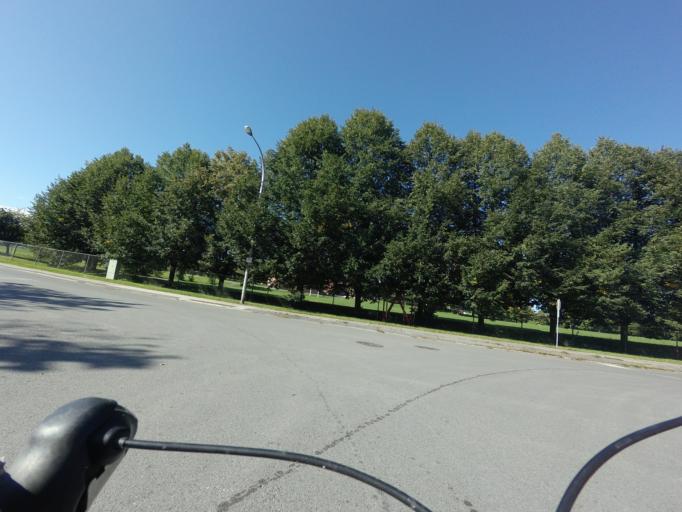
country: CA
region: Ontario
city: Bells Corners
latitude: 45.3157
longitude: -75.8325
